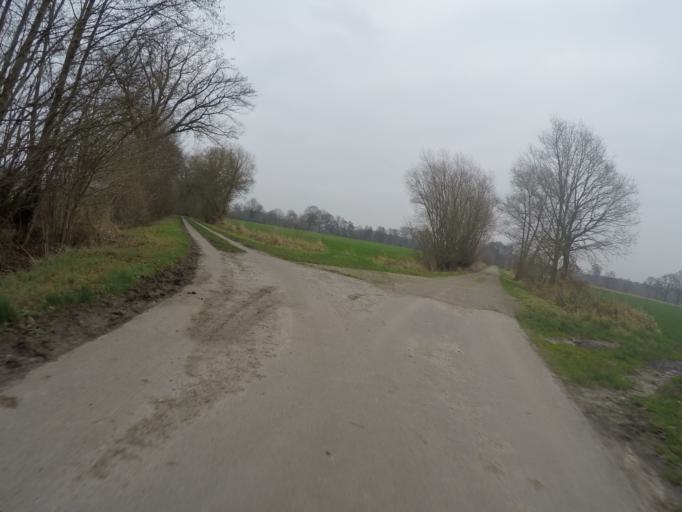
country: DE
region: Schleswig-Holstein
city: Borstel-Hohenraden
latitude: 53.7012
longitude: 9.8343
